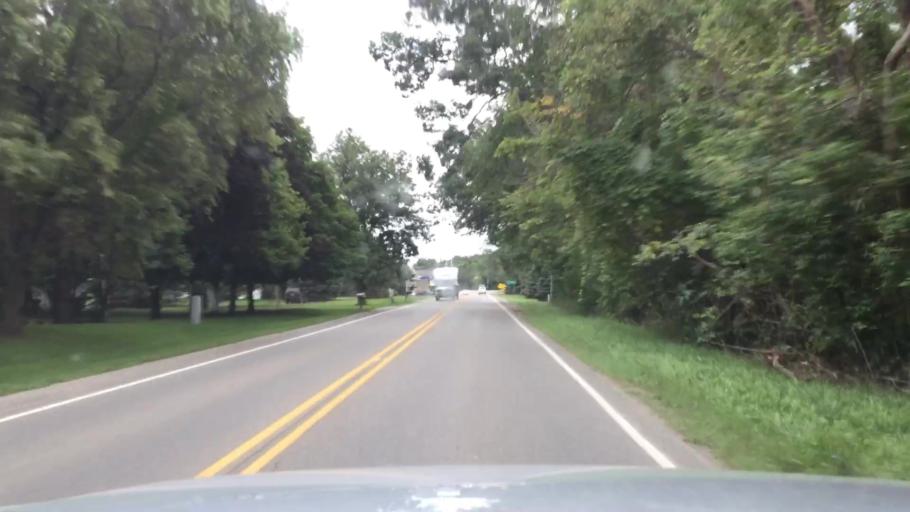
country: US
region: Michigan
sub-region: Genesee County
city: Argentine
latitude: 42.7924
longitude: -83.8504
